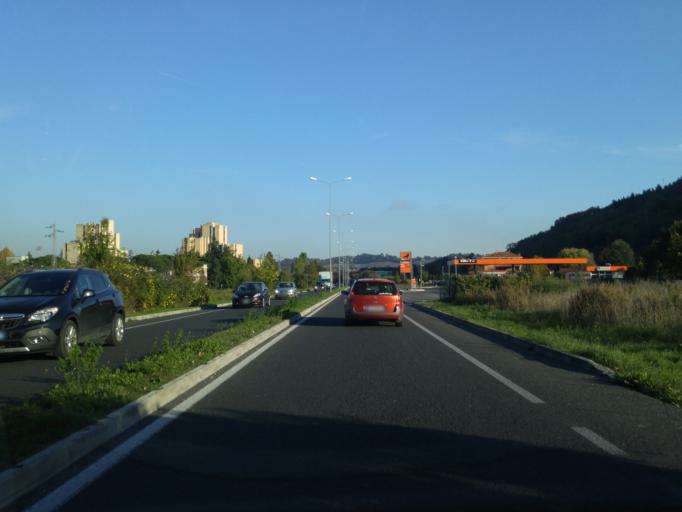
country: IT
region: The Marches
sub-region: Provincia di Pesaro e Urbino
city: Pesaro
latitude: 43.8912
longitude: 12.8894
